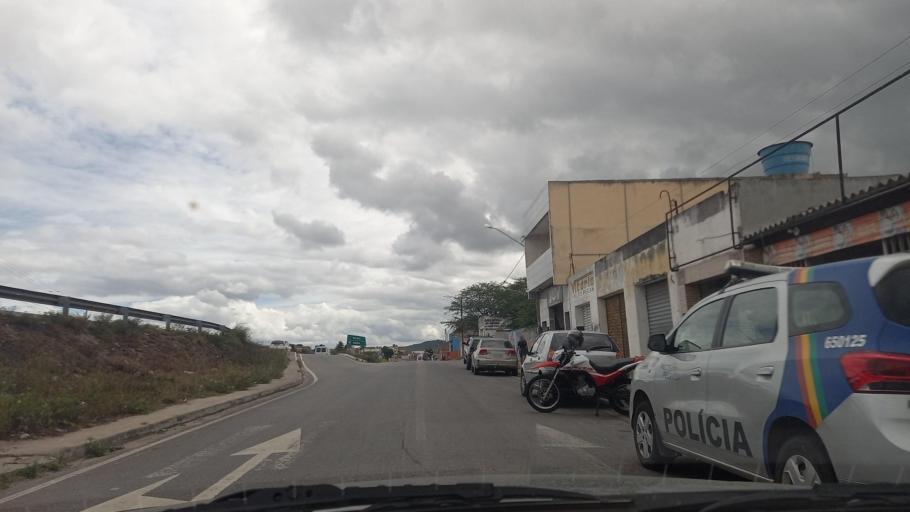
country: BR
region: Pernambuco
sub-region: Caruaru
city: Caruaru
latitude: -8.3327
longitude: -36.1302
